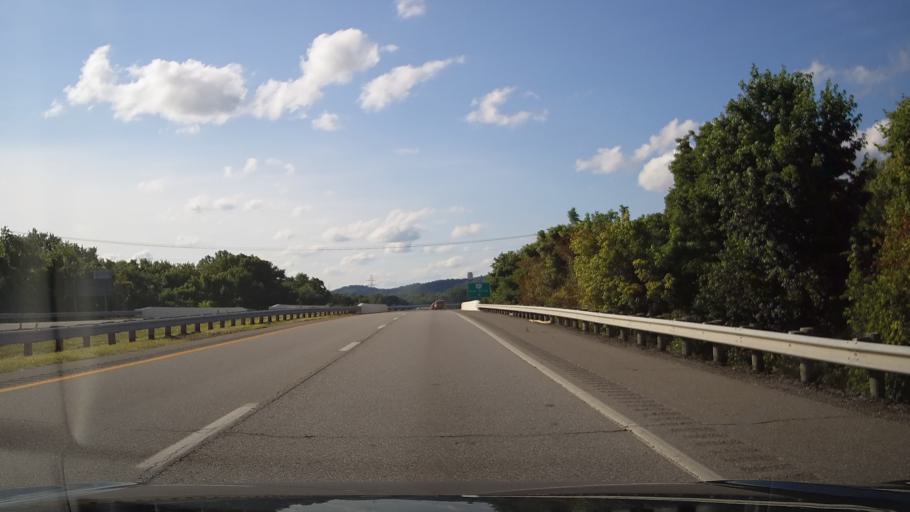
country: US
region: Ohio
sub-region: Lawrence County
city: Coal Grove
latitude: 38.4945
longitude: -82.6477
